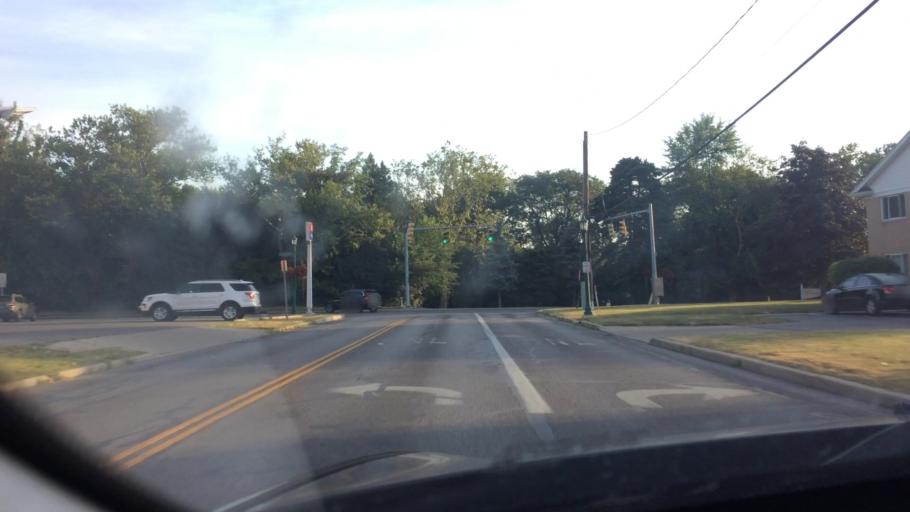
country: US
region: Ohio
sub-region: Lucas County
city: Ottawa Hills
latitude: 41.6620
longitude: -83.6410
